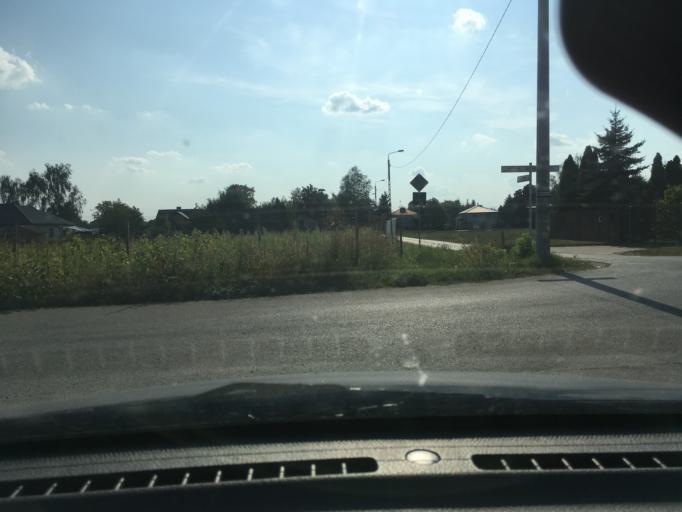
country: PL
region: Masovian Voivodeship
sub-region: Powiat piaseczynski
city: Lesznowola
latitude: 52.0509
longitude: 20.9330
